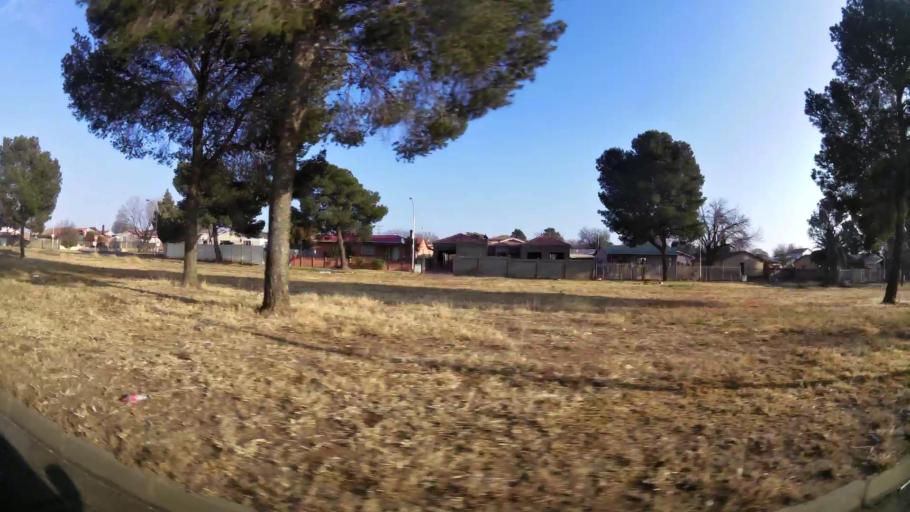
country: ZA
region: Orange Free State
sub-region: Mangaung Metropolitan Municipality
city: Bloemfontein
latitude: -29.1644
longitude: 26.2011
